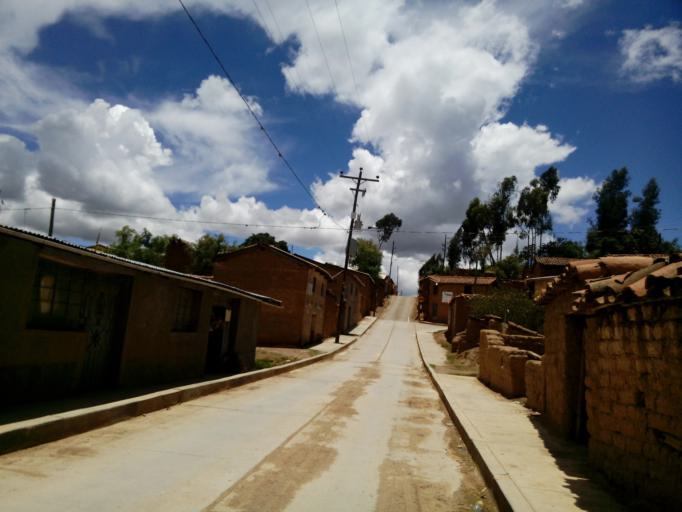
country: PE
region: Ayacucho
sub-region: Provincia de Victor Fajardo
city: Canaria
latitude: -13.8780
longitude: -73.9341
